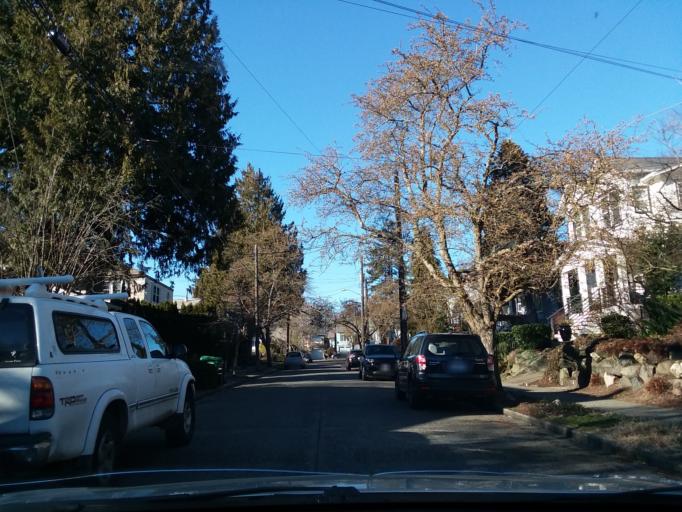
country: US
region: Washington
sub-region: King County
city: Shoreline
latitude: 47.6809
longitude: -122.3584
